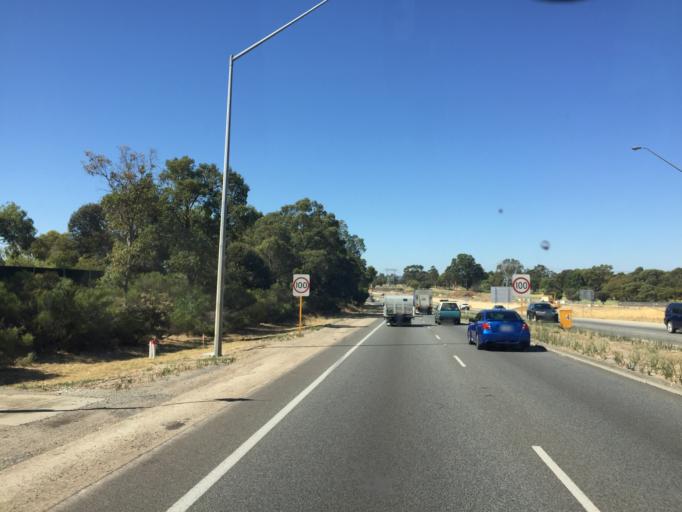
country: AU
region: Western Australia
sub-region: Kalamunda
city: Maida Vale
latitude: -31.9396
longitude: 116.0165
